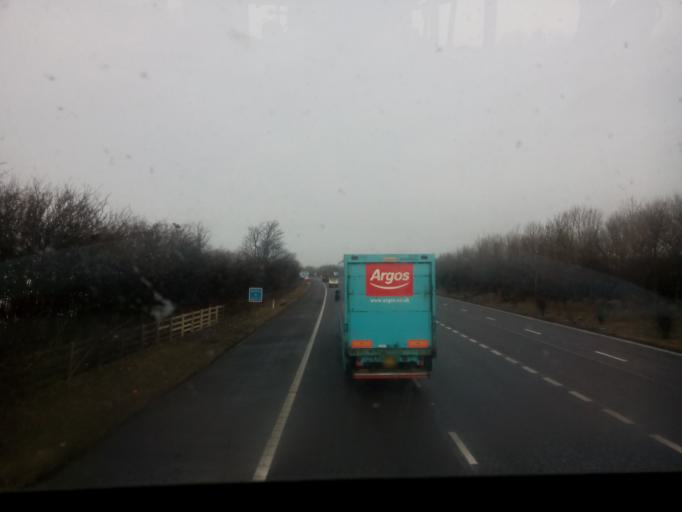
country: GB
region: England
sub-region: County Durham
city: Chester-le-Street
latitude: 54.8983
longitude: -1.5595
